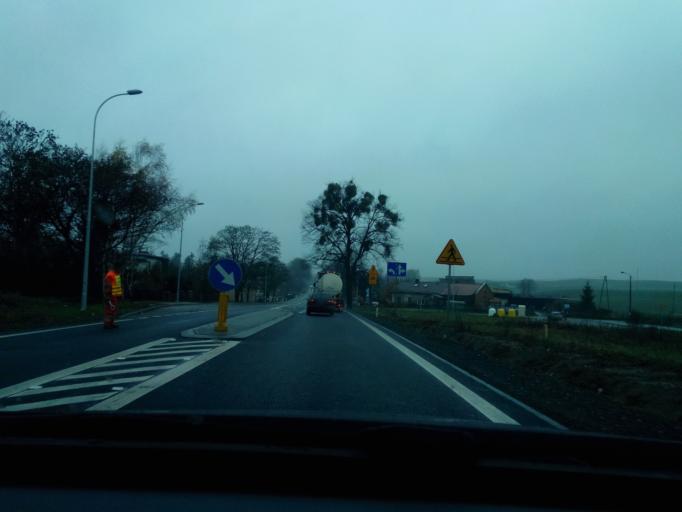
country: PL
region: Pomeranian Voivodeship
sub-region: Powiat tczewski
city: Subkowy
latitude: 54.0471
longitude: 18.7381
